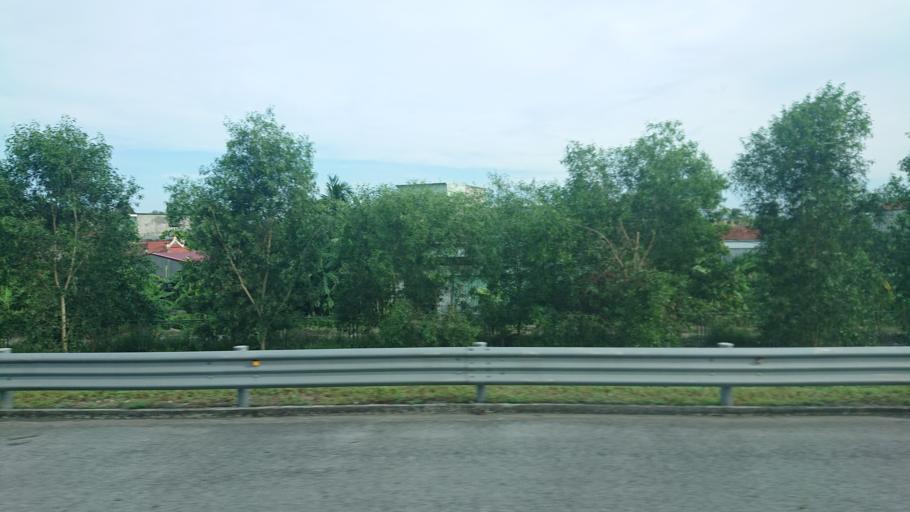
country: VN
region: Hai Phong
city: Nui Doi
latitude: 20.7654
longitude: 106.6662
